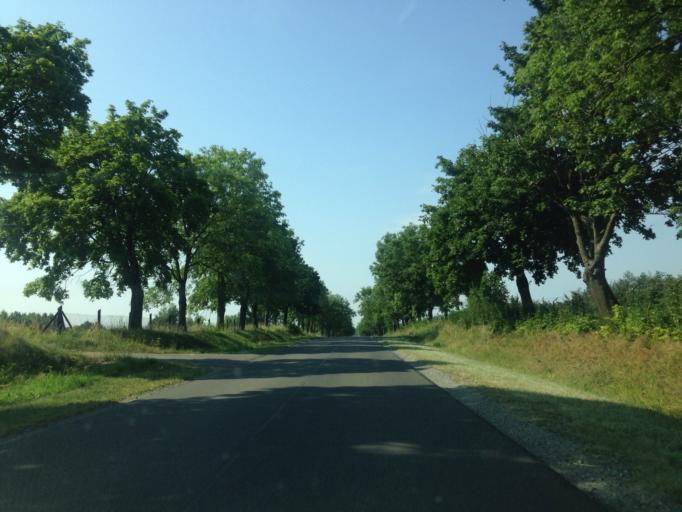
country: PL
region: Kujawsko-Pomorskie
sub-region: Powiat brodnicki
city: Swiedziebnia
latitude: 53.1383
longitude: 19.5360
